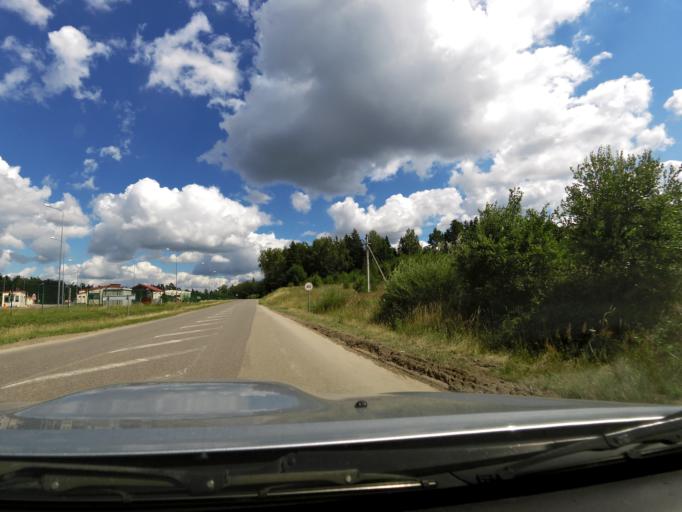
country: LT
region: Vilnius County
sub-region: Vilniaus Rajonas
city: Vievis
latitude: 54.8050
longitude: 24.8194
